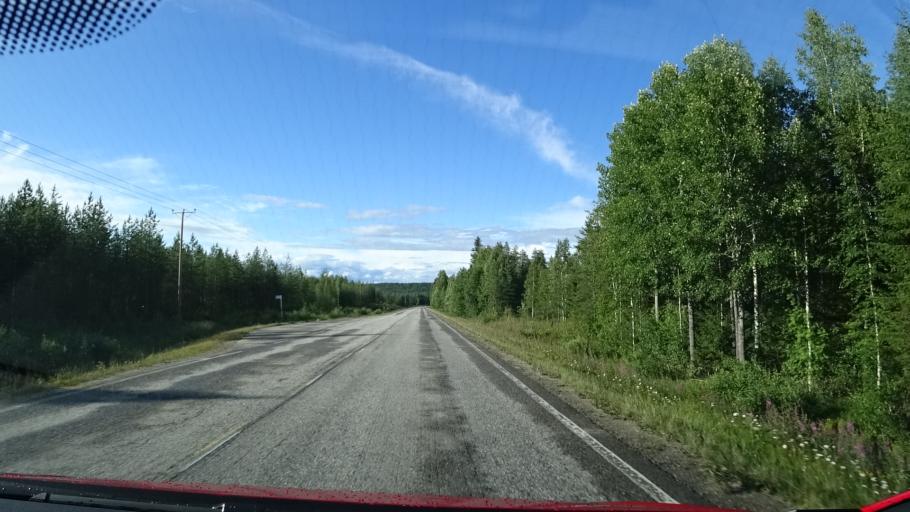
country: FI
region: Kainuu
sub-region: Kehys-Kainuu
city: Kuhmo
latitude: 64.1519
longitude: 29.6338
